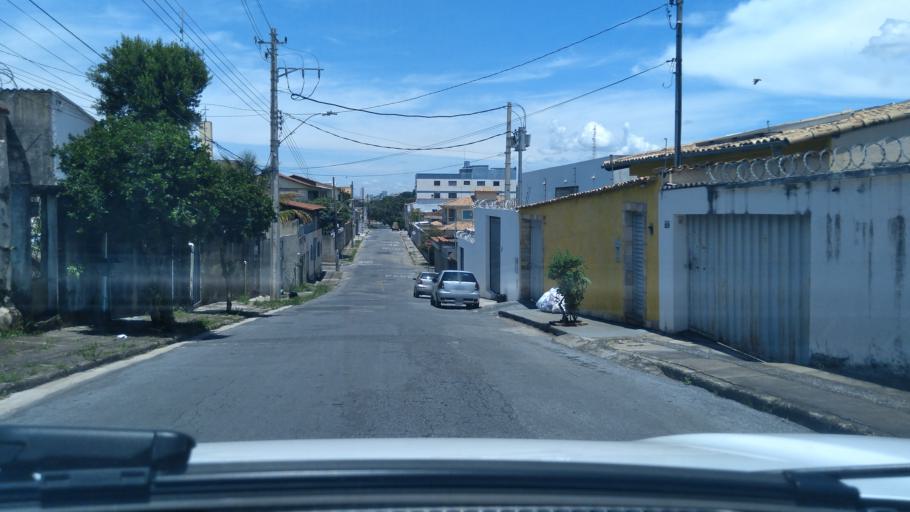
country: BR
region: Minas Gerais
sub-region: Contagem
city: Contagem
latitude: -19.9345
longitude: -43.9995
